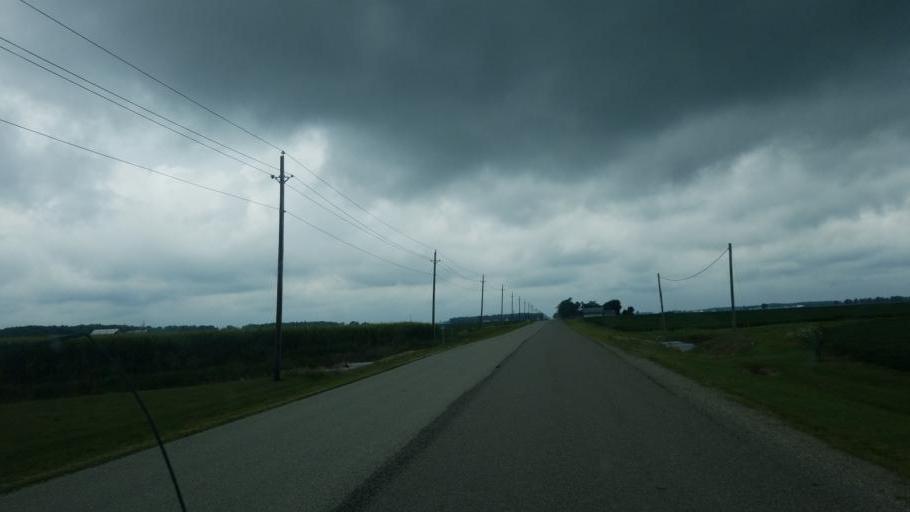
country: US
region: Indiana
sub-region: Wells County
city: Bluffton
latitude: 40.6555
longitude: -85.0834
